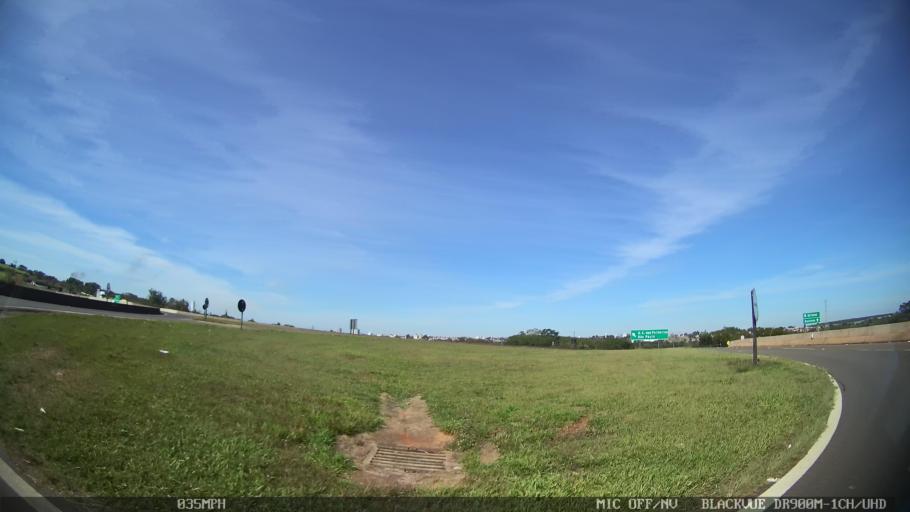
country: BR
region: Sao Paulo
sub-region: Porto Ferreira
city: Porto Ferreira
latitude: -21.8348
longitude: -47.4965
